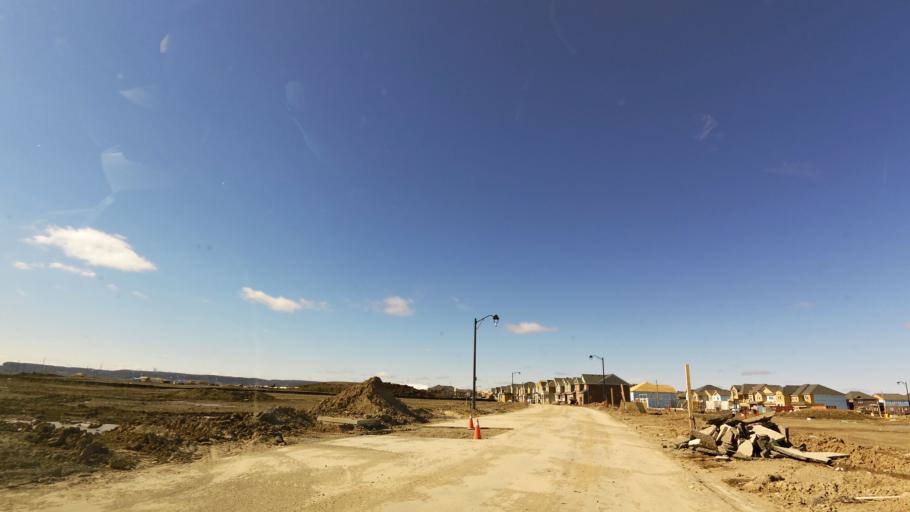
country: CA
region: Ontario
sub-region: Halton
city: Milton
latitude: 43.4834
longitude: -79.8463
